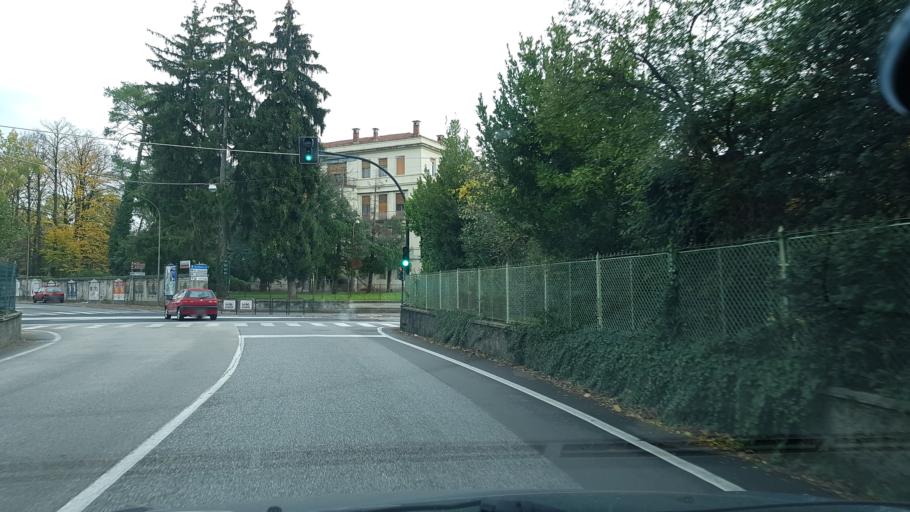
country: IT
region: Friuli Venezia Giulia
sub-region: Provincia di Gorizia
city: Gorizia
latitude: 45.9350
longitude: 13.6305
